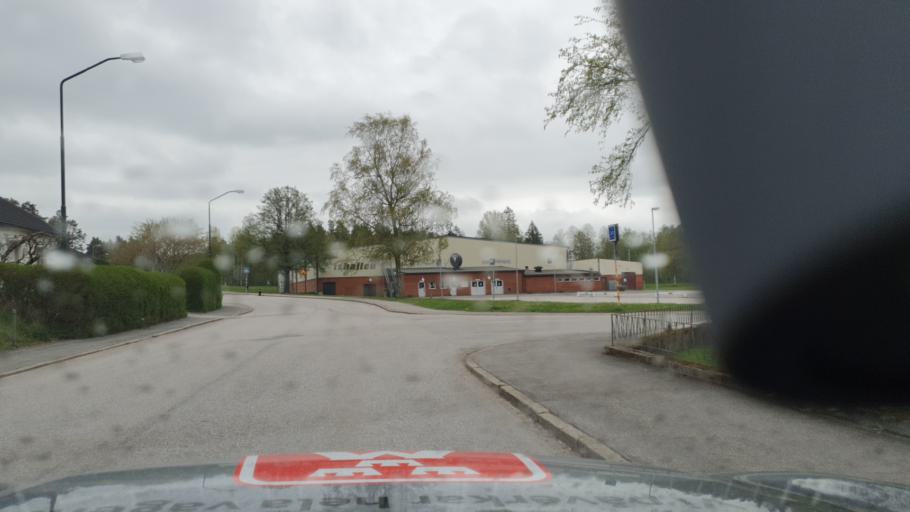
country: SE
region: Kalmar
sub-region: Vimmerby Kommun
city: Vimmerby
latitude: 57.6715
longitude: 15.8690
